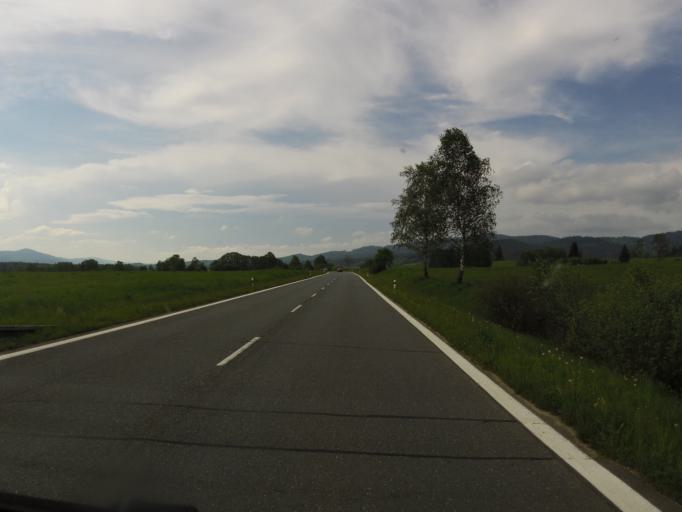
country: CZ
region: Jihocesky
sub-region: Okres Prachatice
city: Volary
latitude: 48.8385
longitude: 13.9482
